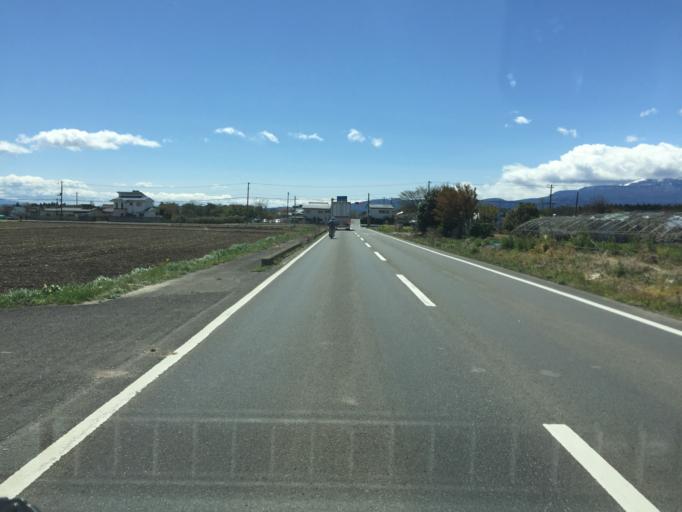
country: JP
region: Fukushima
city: Fukushima-shi
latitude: 37.7892
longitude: 140.4100
